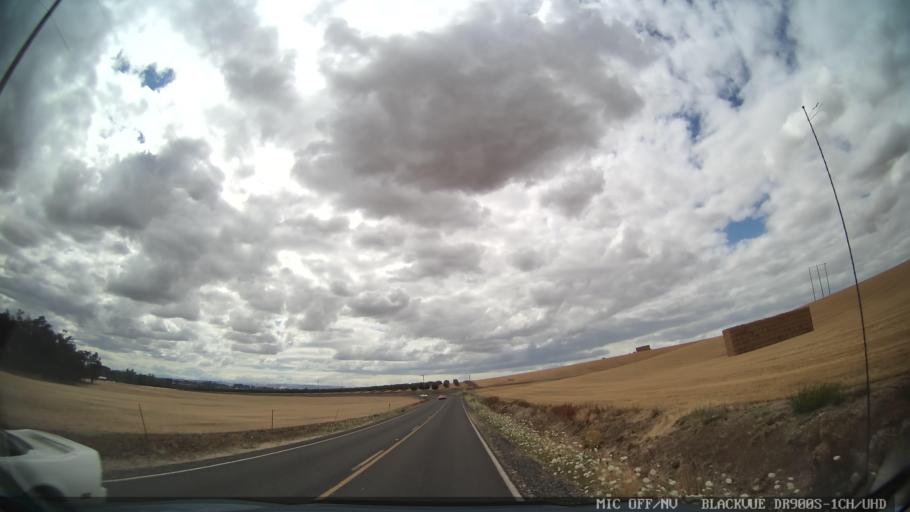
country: US
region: Oregon
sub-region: Marion County
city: Sublimity
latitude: 44.8478
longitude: -122.7508
